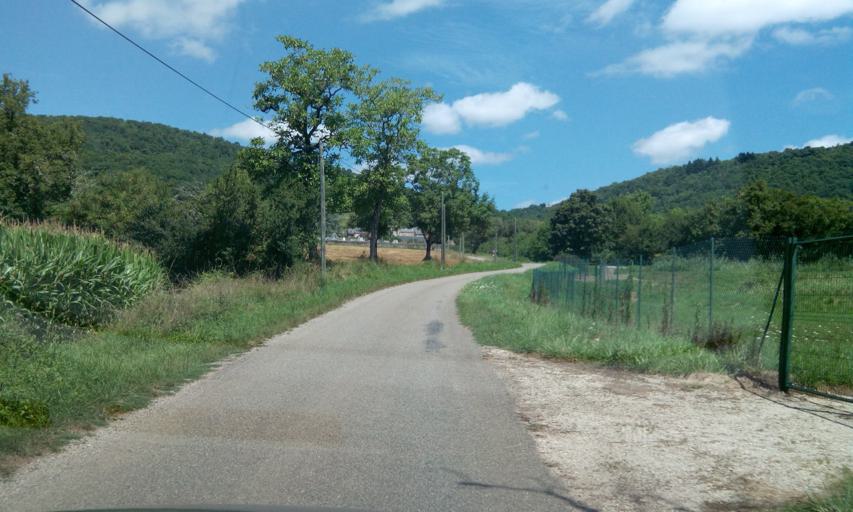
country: FR
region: Limousin
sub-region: Departement de la Correze
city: Meyssac
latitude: 45.0687
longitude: 1.6154
